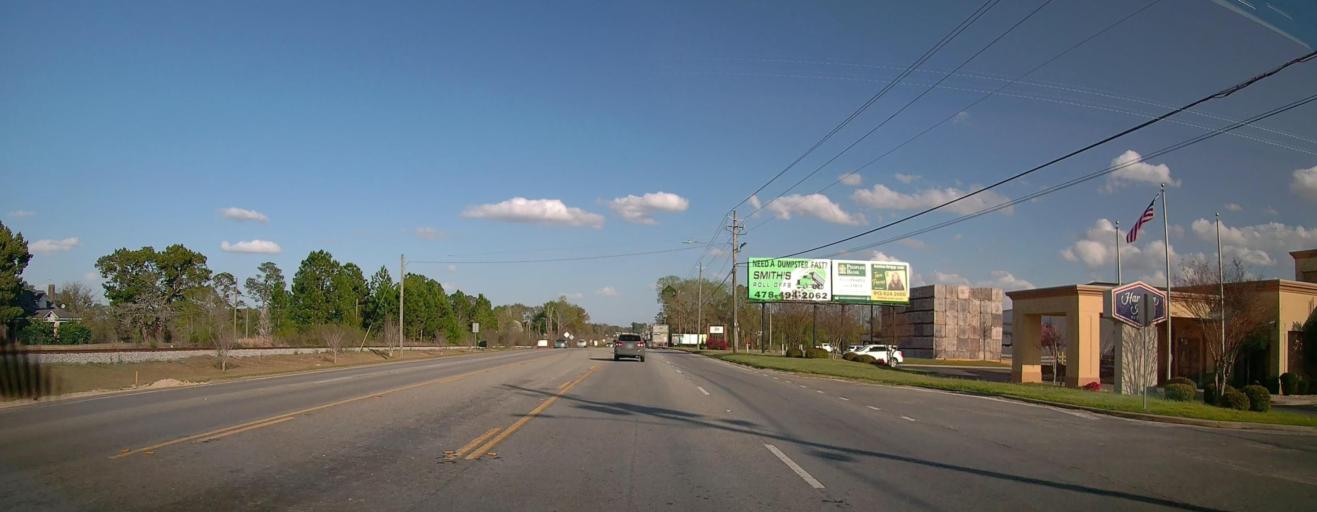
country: US
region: Georgia
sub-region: Toombs County
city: Lyons
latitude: 32.2038
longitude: -82.3548
